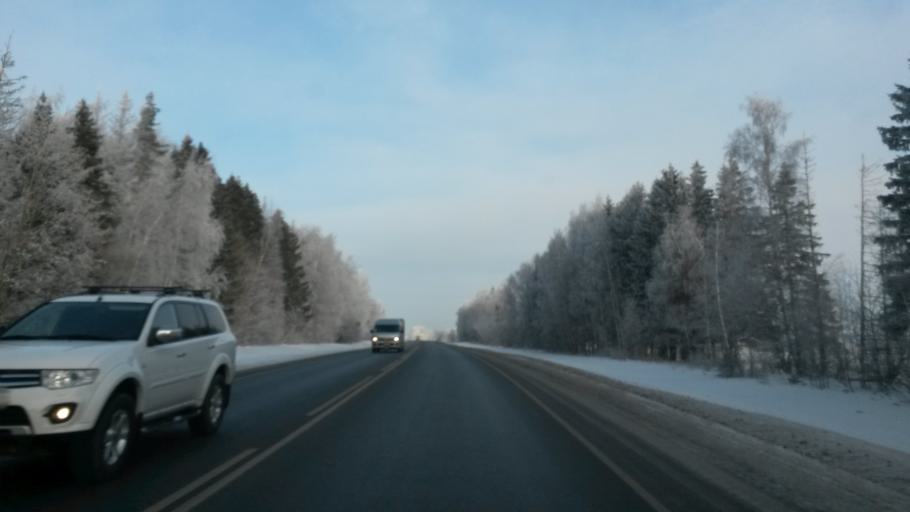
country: RU
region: Vladimir
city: Bogolyubovo
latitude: 56.2355
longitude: 40.4498
